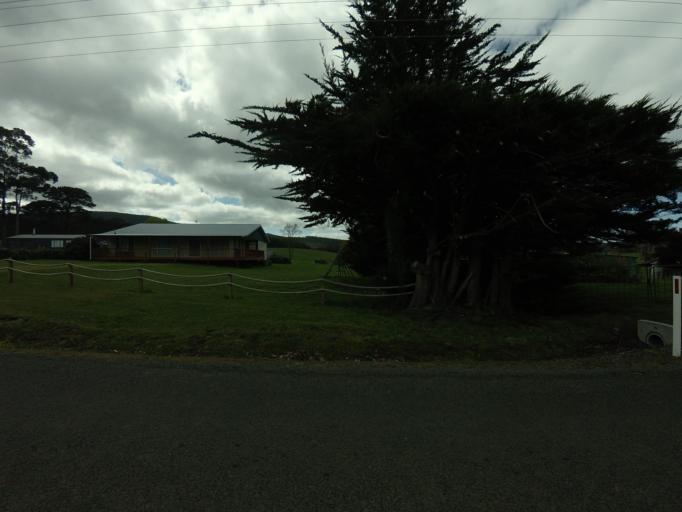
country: AU
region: Tasmania
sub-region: Huon Valley
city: Geeveston
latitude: -43.4341
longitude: 146.9800
